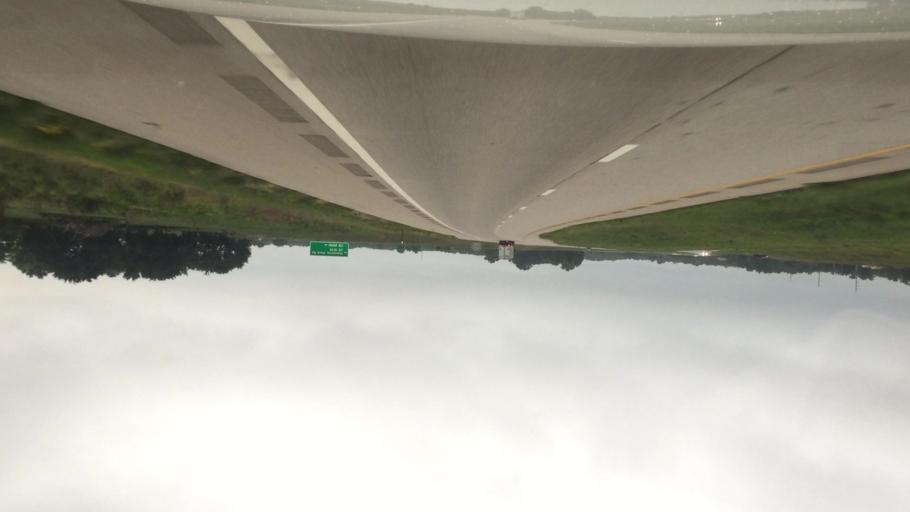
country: US
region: Kansas
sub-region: Montgomery County
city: Coffeyville
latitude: 37.0774
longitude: -95.5896
